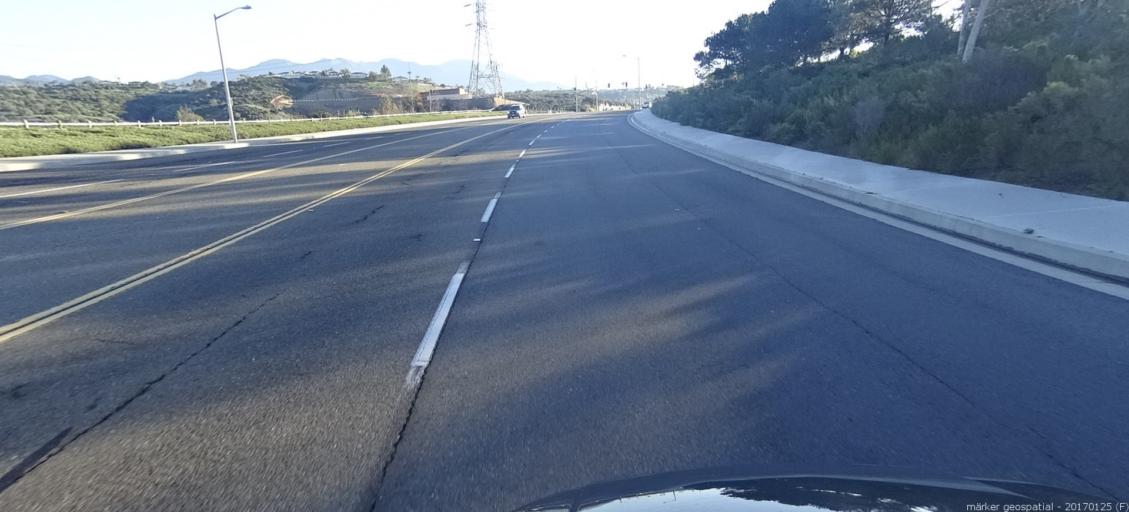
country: US
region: California
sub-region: Orange County
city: Portola Hills
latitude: 33.6735
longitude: -117.6469
